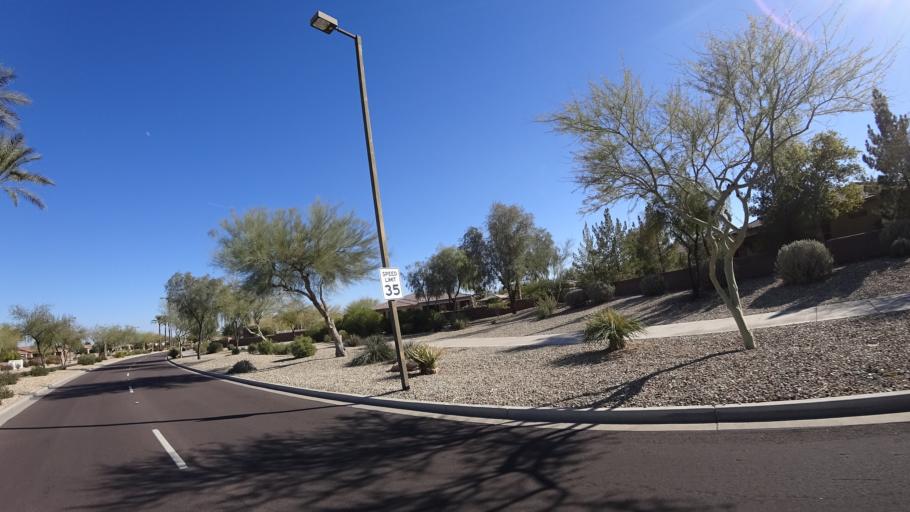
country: US
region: Arizona
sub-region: Maricopa County
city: Sun City West
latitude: 33.6729
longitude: -112.4162
